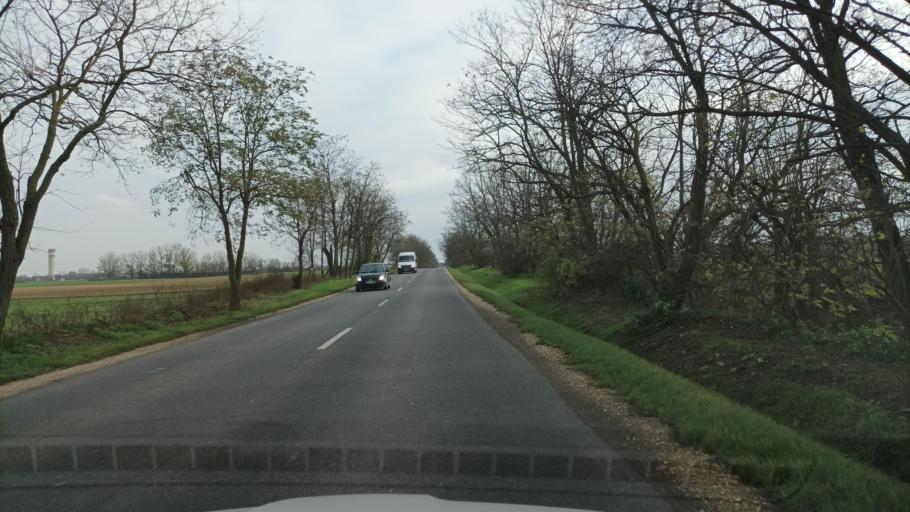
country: HU
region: Pest
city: Ocsa
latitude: 47.3128
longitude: 19.2065
